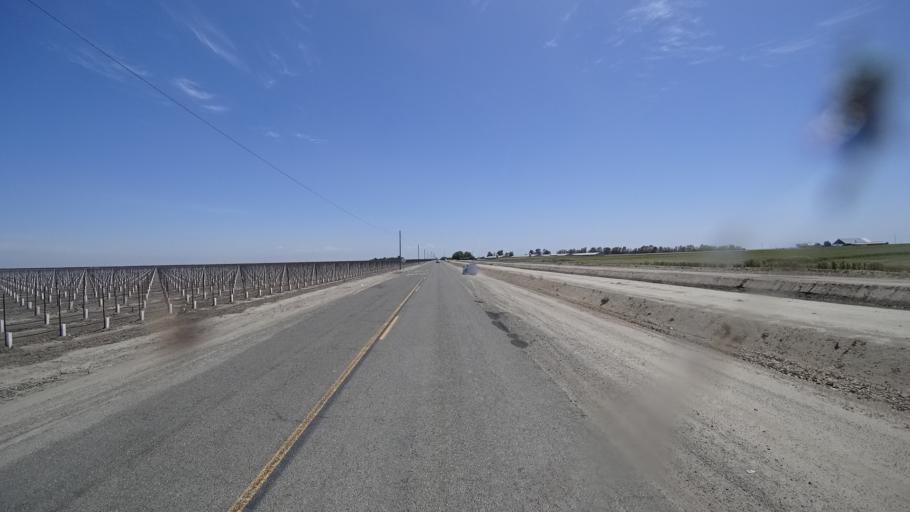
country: US
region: California
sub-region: Kings County
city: Corcoran
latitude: 36.1162
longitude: -119.6433
